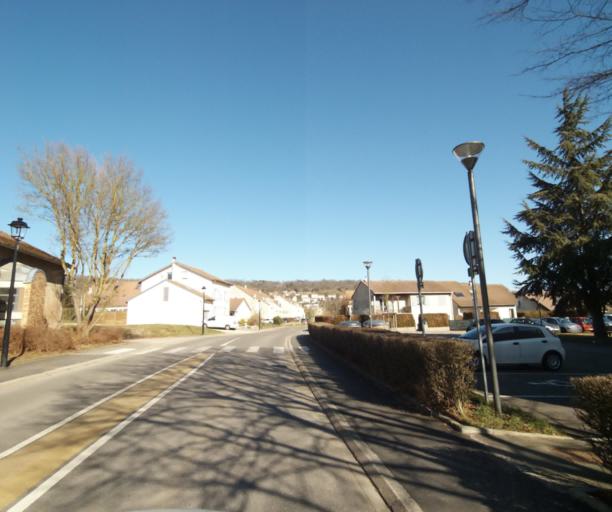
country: FR
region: Lorraine
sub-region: Departement de Meurthe-et-Moselle
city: Ludres
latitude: 48.6178
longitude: 6.1590
